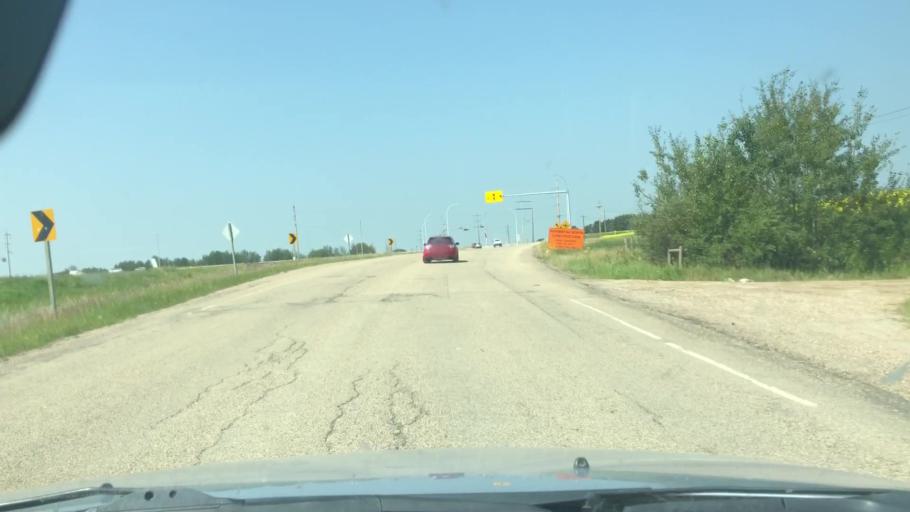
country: CA
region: Alberta
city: Devon
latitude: 53.5122
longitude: -113.7576
